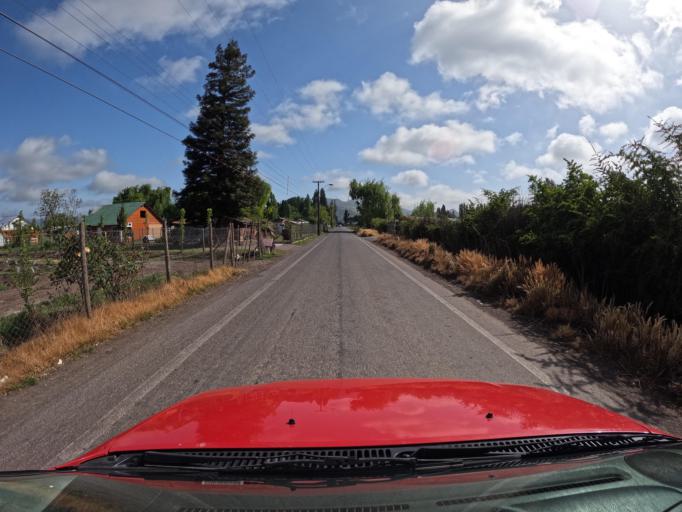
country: CL
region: Maule
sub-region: Provincia de Curico
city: Teno
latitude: -34.8763
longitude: -71.2259
